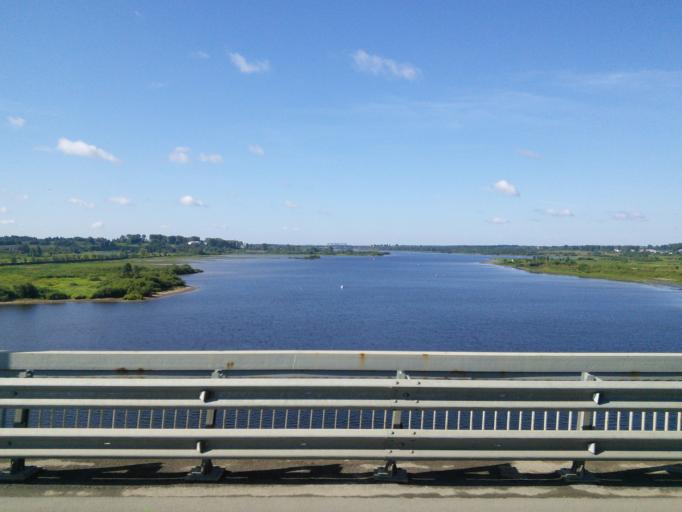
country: RU
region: Vologda
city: Sheksna
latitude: 59.2128
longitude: 38.4949
